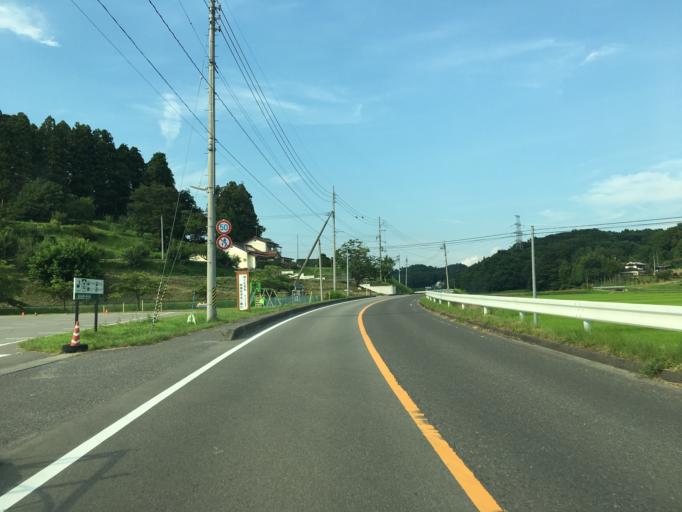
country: JP
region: Fukushima
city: Motomiya
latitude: 37.4950
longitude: 140.4300
